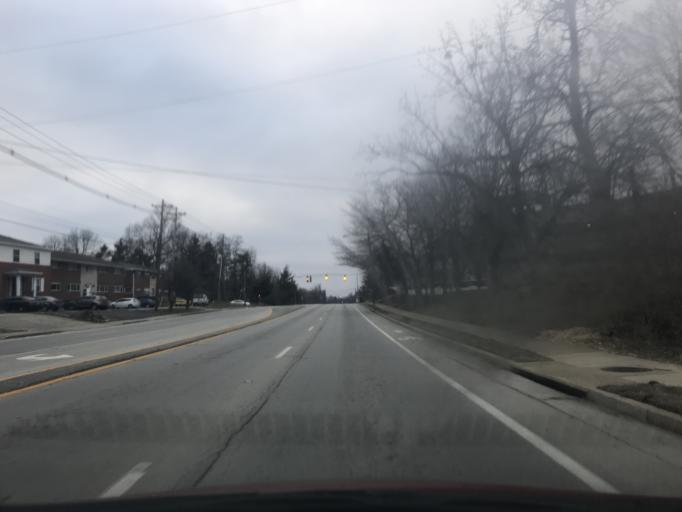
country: US
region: Kentucky
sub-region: Jefferson County
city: Audubon Park
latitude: 38.2132
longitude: -85.7221
